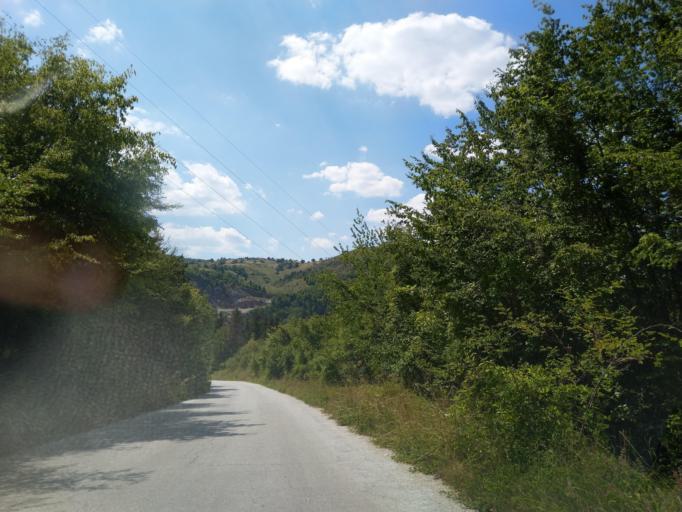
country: RS
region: Central Serbia
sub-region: Zlatiborski Okrug
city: Nova Varos
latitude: 43.4205
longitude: 19.9326
